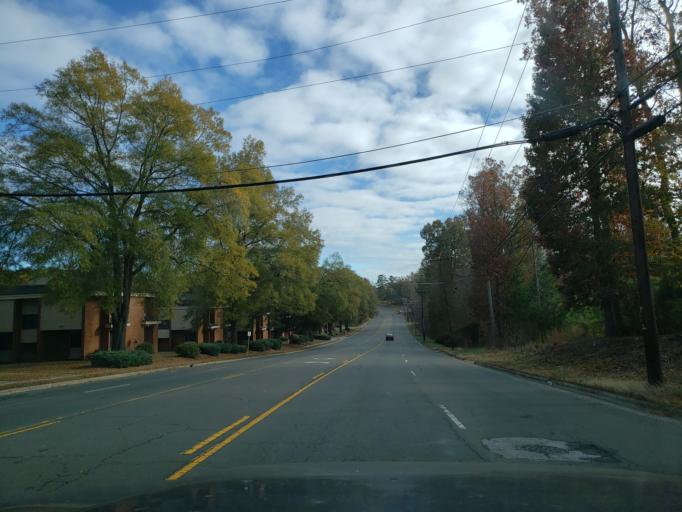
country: US
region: North Carolina
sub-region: Durham County
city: Durham
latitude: 35.9638
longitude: -78.9172
